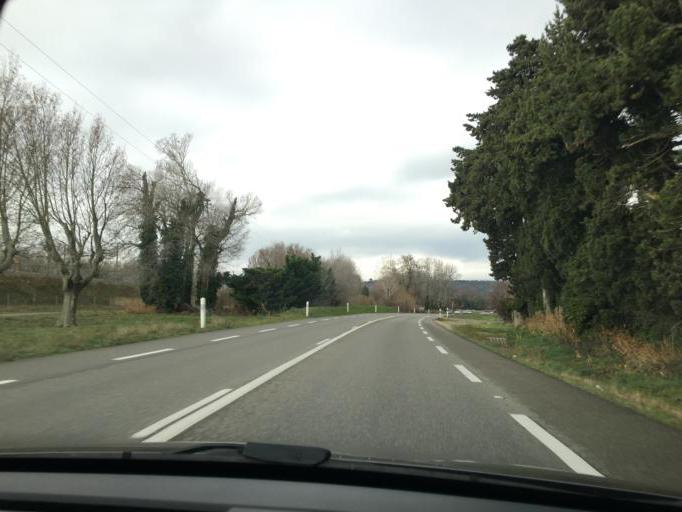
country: FR
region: Provence-Alpes-Cote d'Azur
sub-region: Departement du Vaucluse
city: Caumont-sur-Durance
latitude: 43.8843
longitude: 4.9492
